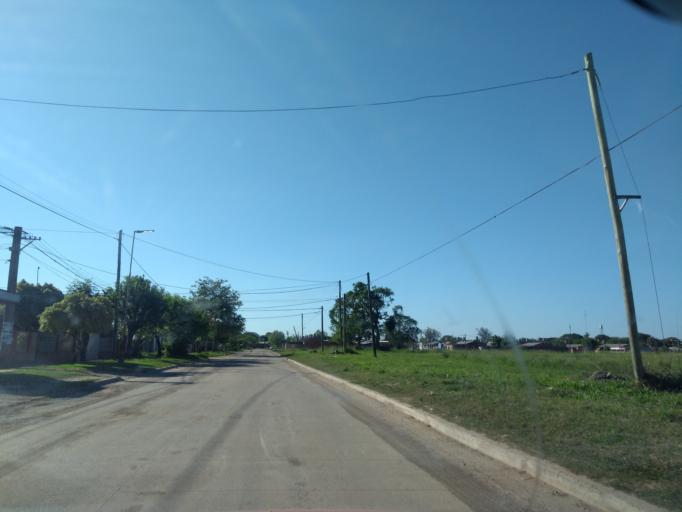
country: AR
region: Chaco
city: Fontana
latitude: -27.4186
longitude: -59.0444
